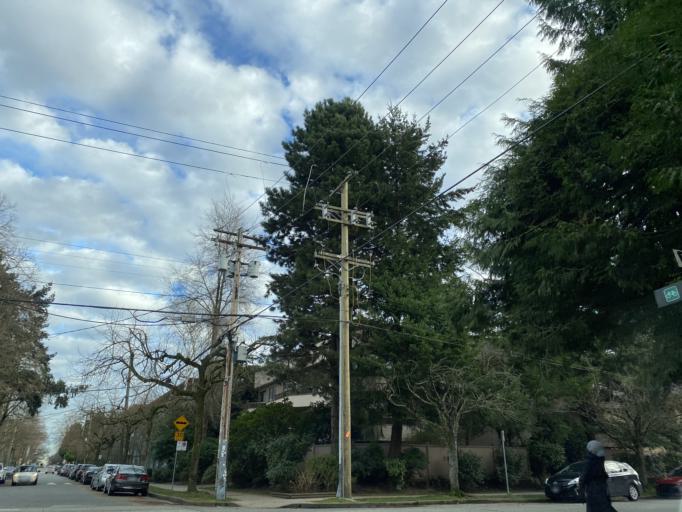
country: CA
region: British Columbia
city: West End
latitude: 49.2648
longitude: -123.1555
